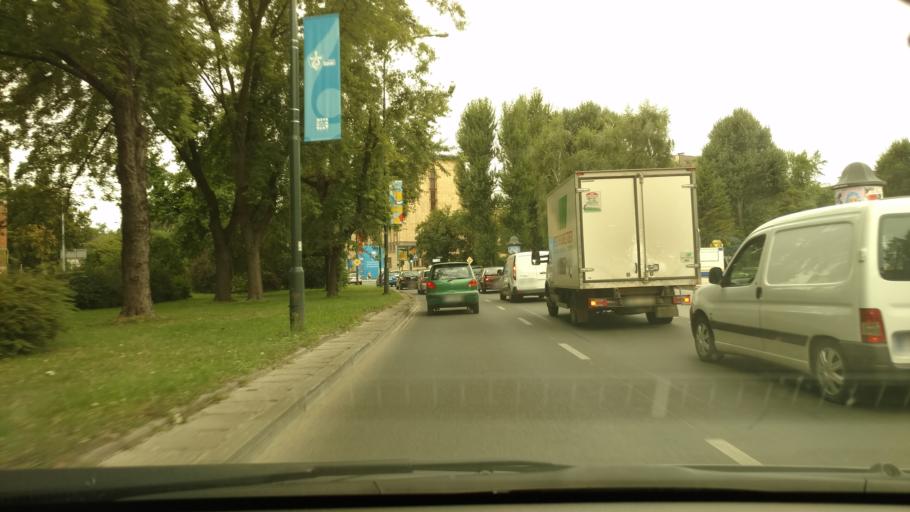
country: PL
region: Lesser Poland Voivodeship
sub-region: Krakow
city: Krakow
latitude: 50.0633
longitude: 19.9234
